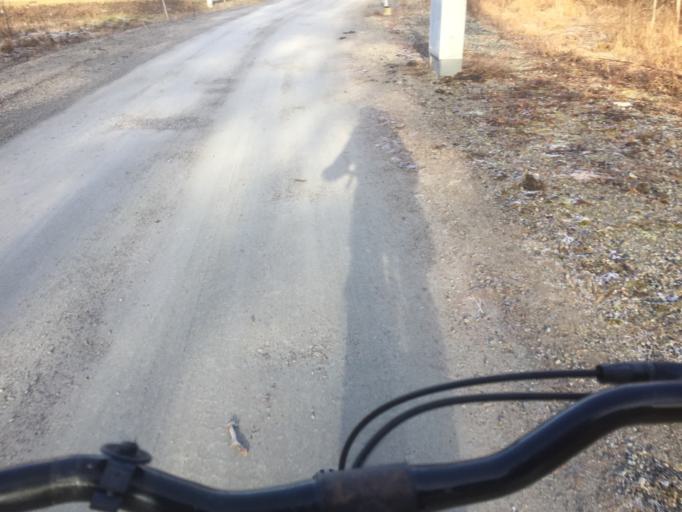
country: SE
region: Joenkoeping
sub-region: Aneby Kommun
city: Aneby
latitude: 57.8233
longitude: 14.8161
